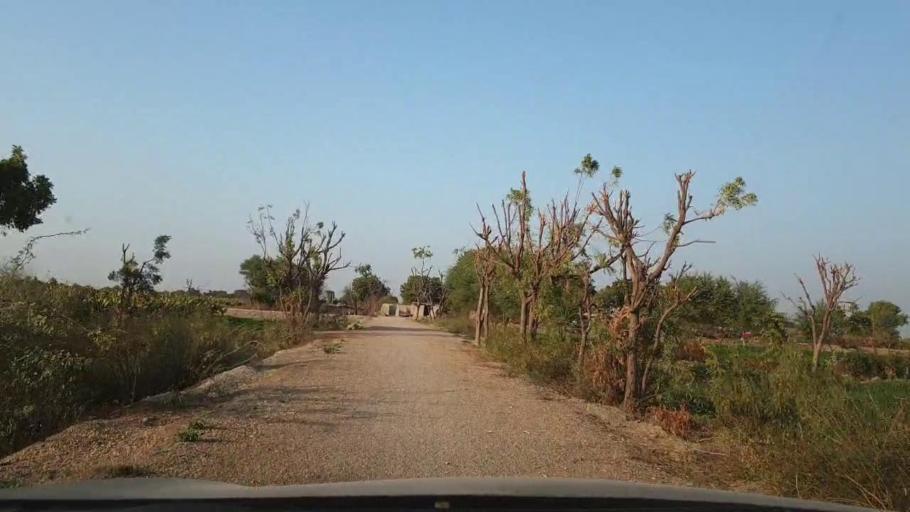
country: PK
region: Sindh
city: Tando Allahyar
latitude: 25.5698
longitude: 68.7932
